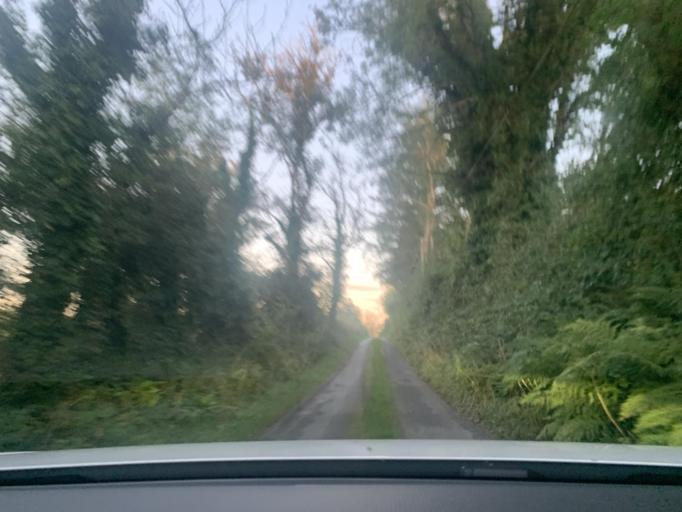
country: IE
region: Connaught
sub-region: Sligo
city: Sligo
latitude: 54.2740
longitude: -8.4145
